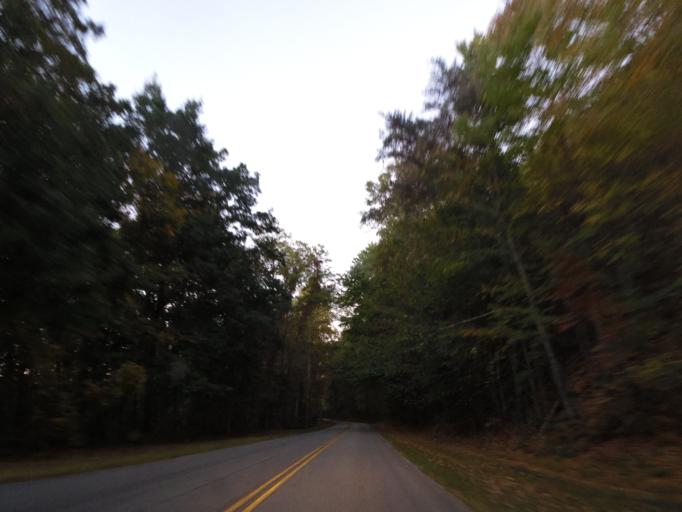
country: US
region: Tennessee
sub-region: Blount County
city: Maryville
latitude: 35.6920
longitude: -83.8811
